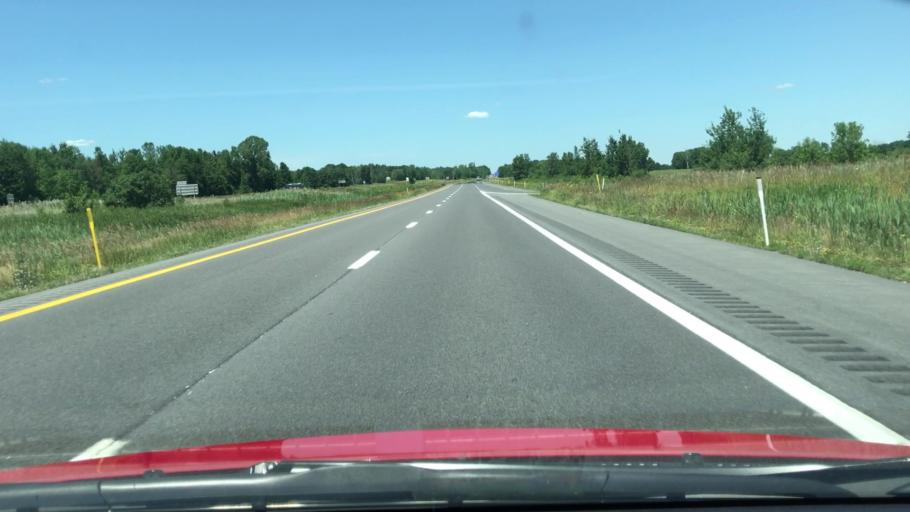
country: US
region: New York
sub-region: Clinton County
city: Cumberland Head
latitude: 44.7824
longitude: -73.4375
